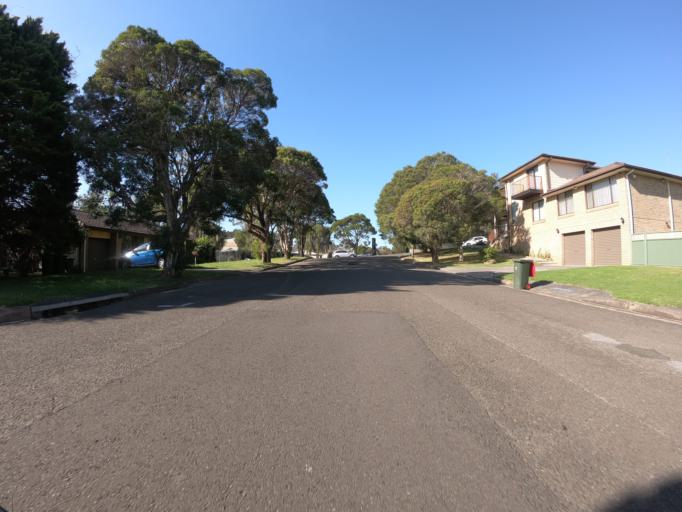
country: AU
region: New South Wales
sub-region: Wollongong
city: Cordeaux Heights
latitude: -34.4401
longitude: 150.8500
